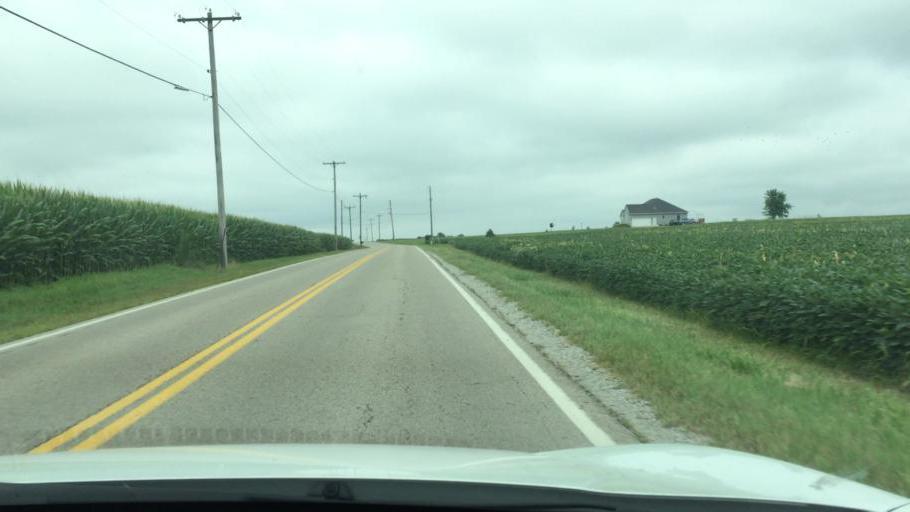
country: US
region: Ohio
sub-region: Clark County
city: Lisbon
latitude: 39.9421
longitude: -83.6411
